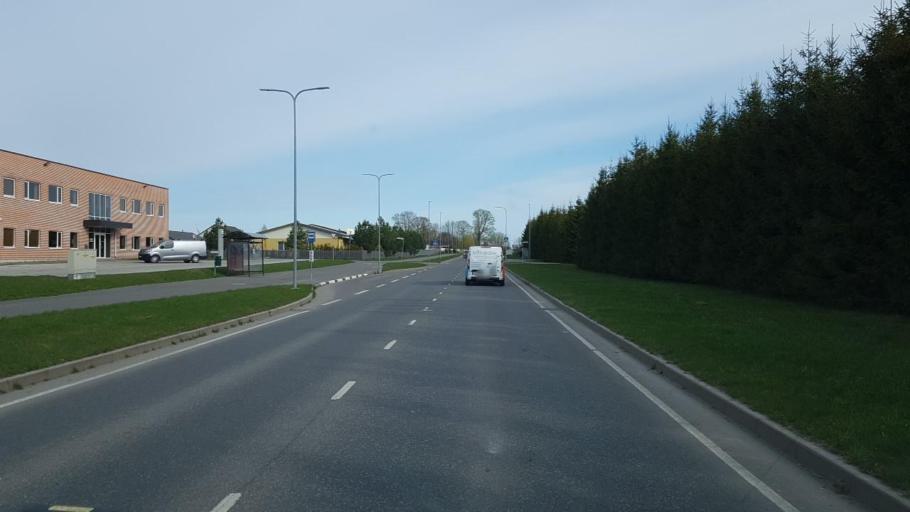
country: EE
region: Tartu
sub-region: UElenurme vald
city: Ulenurme
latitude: 58.3383
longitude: 26.7021
